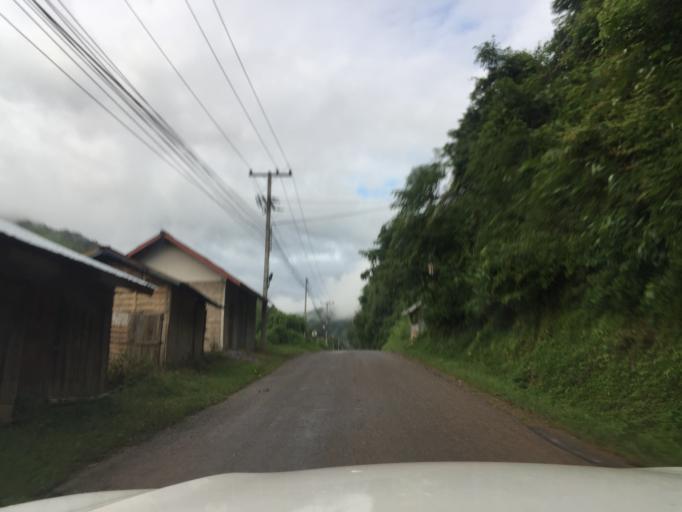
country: LA
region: Phongsali
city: Khoa
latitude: 21.0982
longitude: 102.2522
